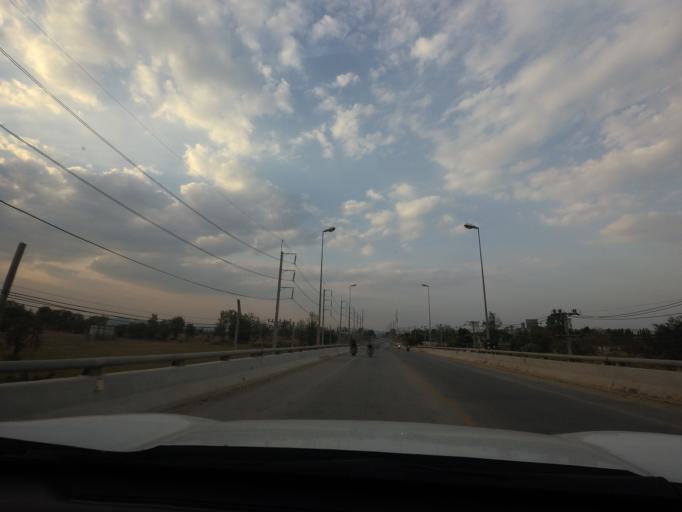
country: TH
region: Nakhon Ratchasima
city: Pak Chong
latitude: 14.6746
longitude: 101.4552
